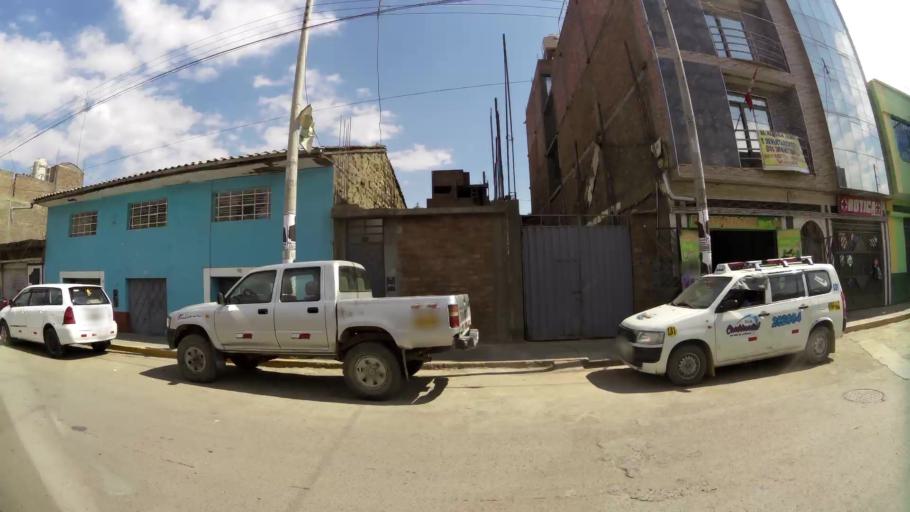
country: PE
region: Junin
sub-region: Provincia de Huancayo
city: Huancayo
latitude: -12.0829
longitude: -75.1971
